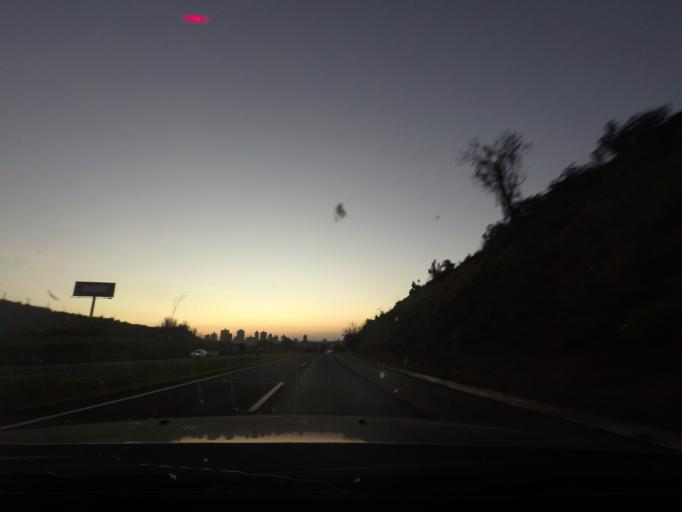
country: BR
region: Sao Paulo
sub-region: Piracicaba
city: Piracicaba
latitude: -22.7204
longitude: -47.6164
